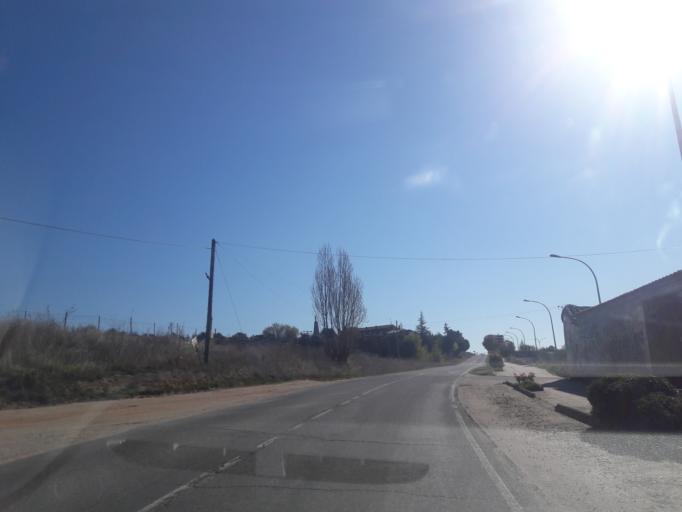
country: ES
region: Castille and Leon
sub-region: Provincia de Salamanca
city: Macotera
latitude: 40.8338
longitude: -5.2828
